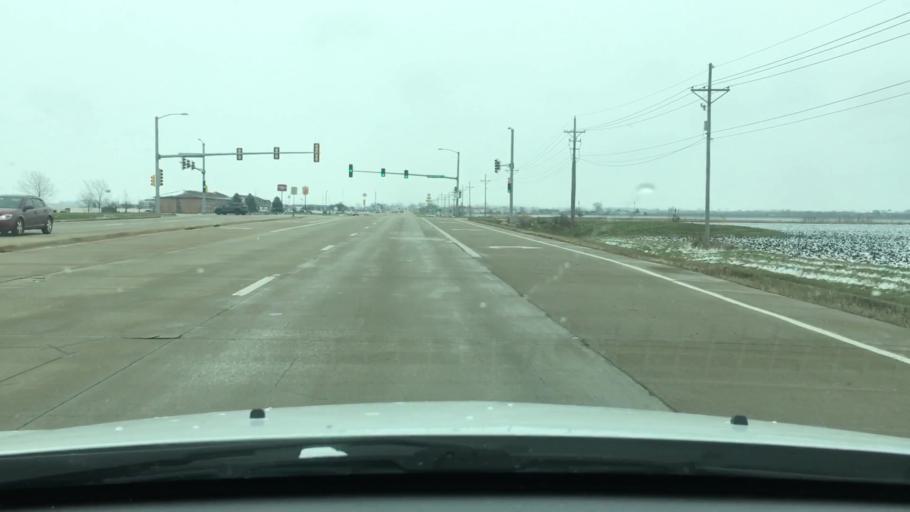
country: US
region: Illinois
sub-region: Ogle County
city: Rochelle
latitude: 41.9342
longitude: -89.0497
